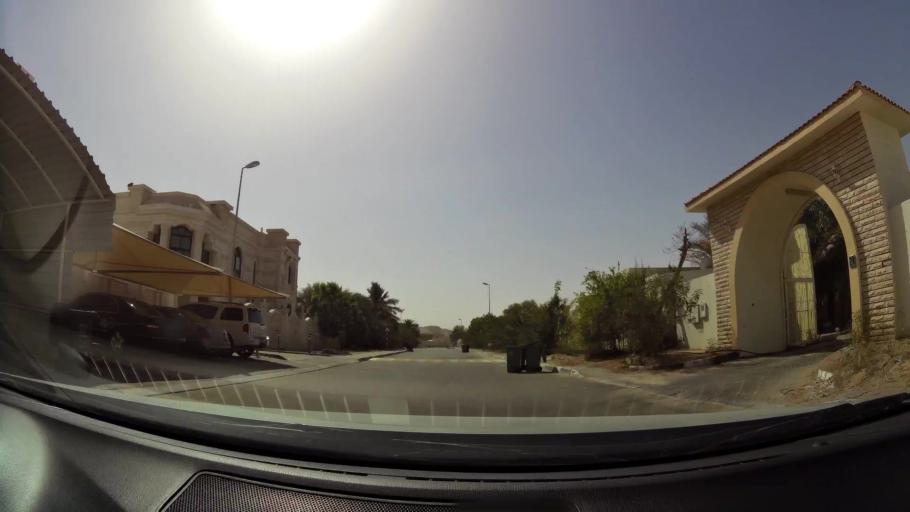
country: OM
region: Al Buraimi
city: Al Buraymi
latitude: 24.3057
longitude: 55.7987
